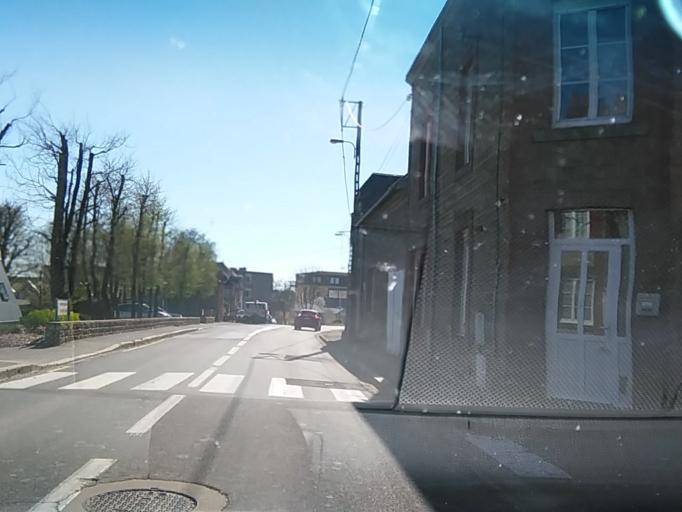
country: FR
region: Lower Normandy
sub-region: Departement de l'Orne
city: La Ferte-Mace
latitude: 48.5880
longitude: -0.3572
